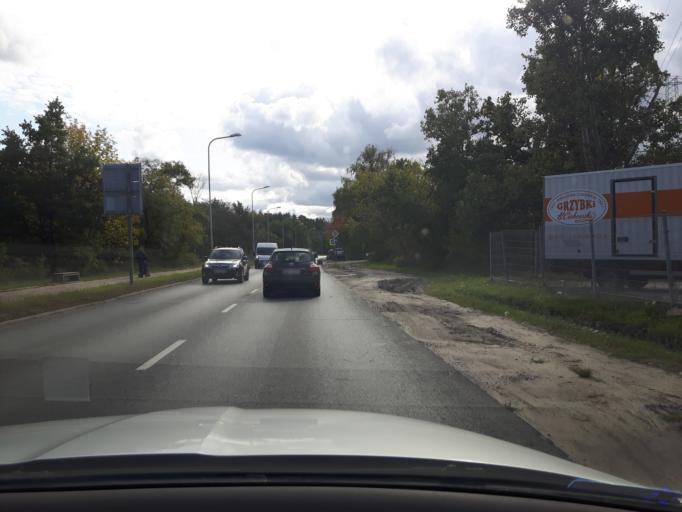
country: PL
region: Masovian Voivodeship
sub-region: Warszawa
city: Rembertow
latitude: 52.2361
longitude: 21.1428
